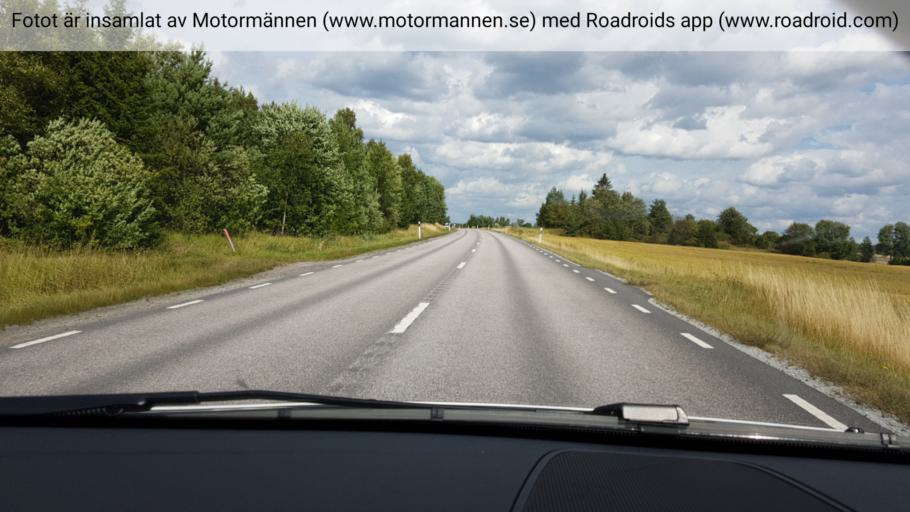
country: SE
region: Stockholm
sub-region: Vallentuna Kommun
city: Vallentuna
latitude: 59.7347
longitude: 18.0563
